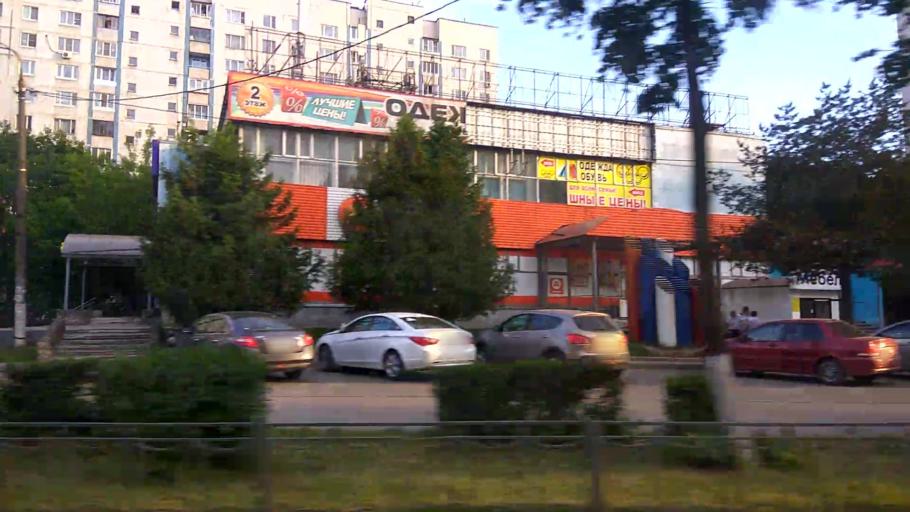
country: RU
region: Moskovskaya
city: Yubileyny
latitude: 55.9226
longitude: 37.8655
